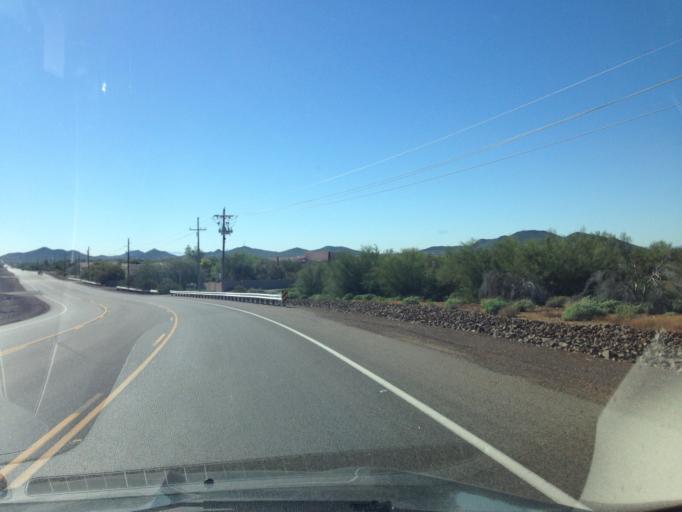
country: US
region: Arizona
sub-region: Maricopa County
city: Anthem
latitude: 33.8412
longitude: -112.0653
